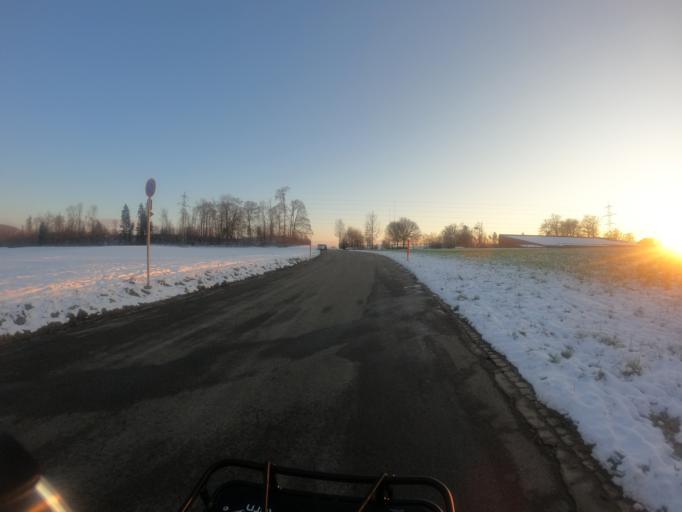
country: CH
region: Zurich
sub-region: Bezirk Affoltern
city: Affoltern / Hasenbueel
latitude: 47.2700
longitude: 8.4503
